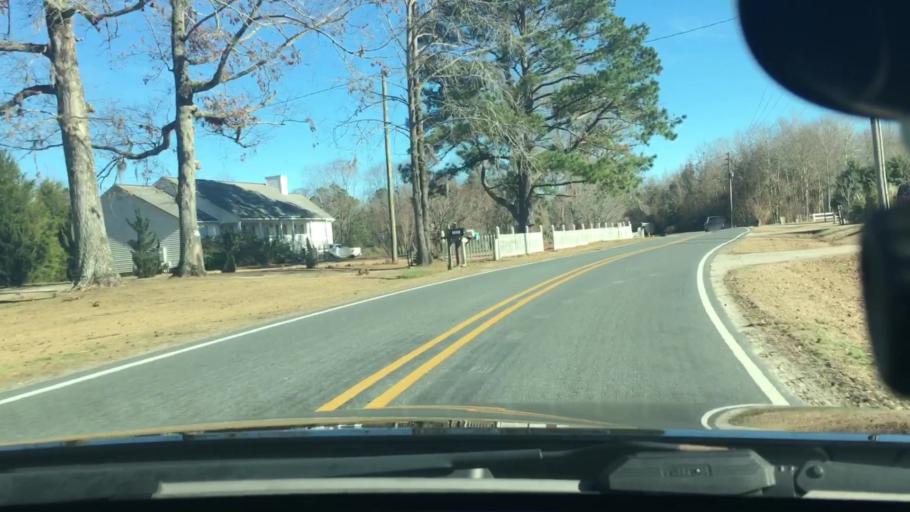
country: US
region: North Carolina
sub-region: Craven County
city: New Bern
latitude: 35.1893
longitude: -77.0579
